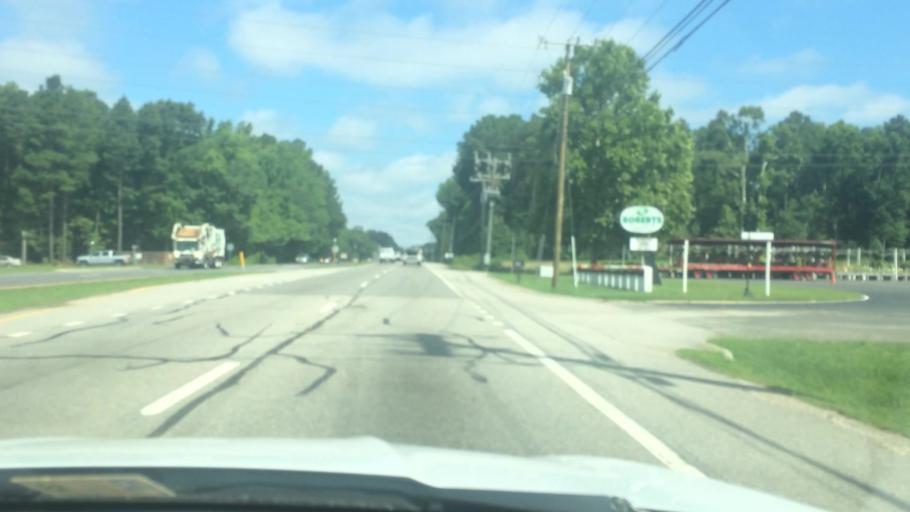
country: US
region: Virginia
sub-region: York County
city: Yorktown
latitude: 37.1845
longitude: -76.4841
